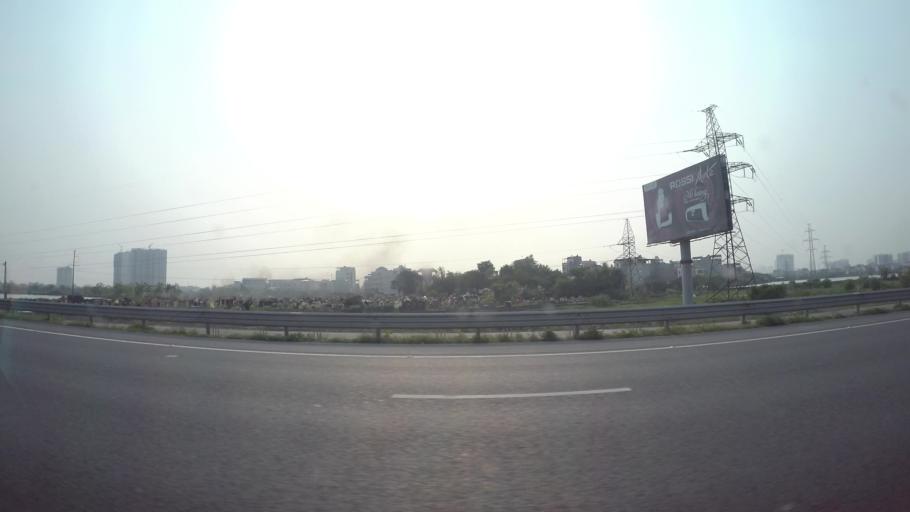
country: VN
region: Ha Noi
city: Van Dien
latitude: 20.9394
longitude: 105.8595
